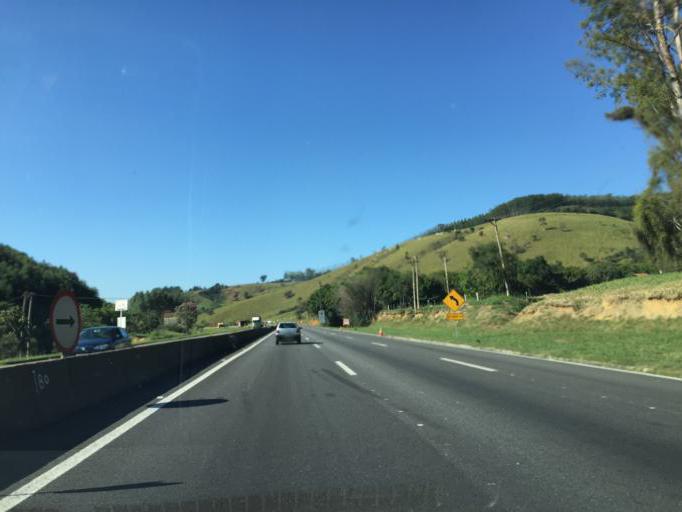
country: BR
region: Sao Paulo
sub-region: Aparecida
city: Aparecida
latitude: -22.8727
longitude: -45.2504
